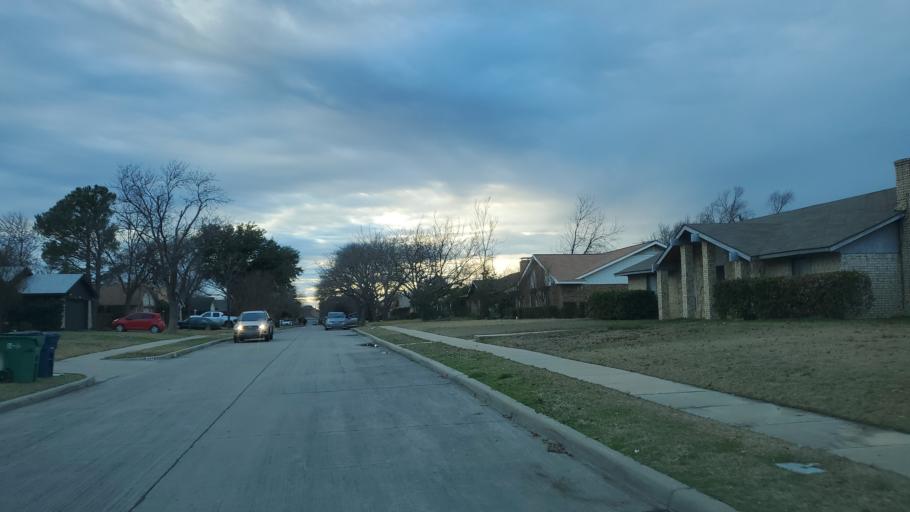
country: US
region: Texas
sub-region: Dallas County
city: Carrollton
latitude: 32.9919
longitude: -96.8847
